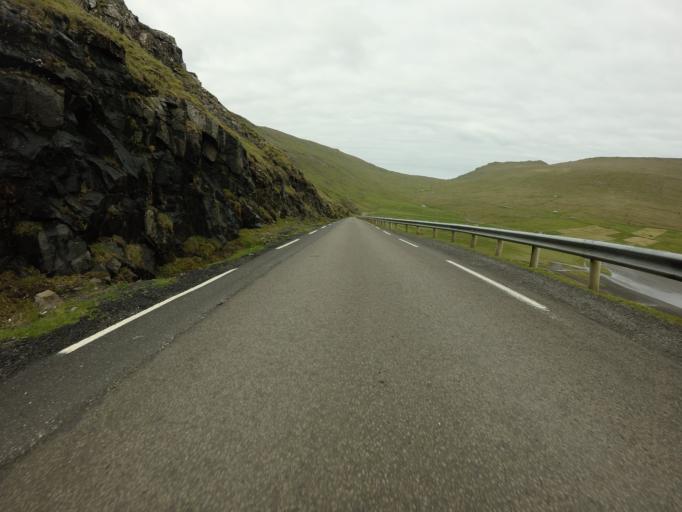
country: FO
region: Suduroy
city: Tvoroyri
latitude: 61.6239
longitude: -6.9337
